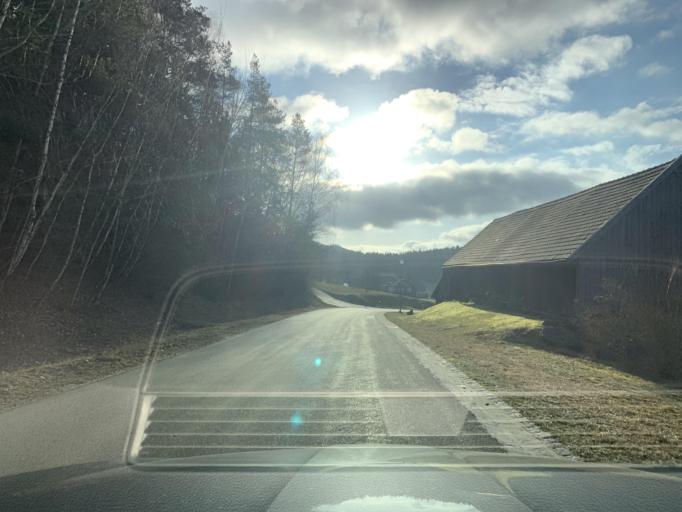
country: DE
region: Bavaria
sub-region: Upper Palatinate
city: Thanstein
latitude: 49.3704
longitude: 12.4371
